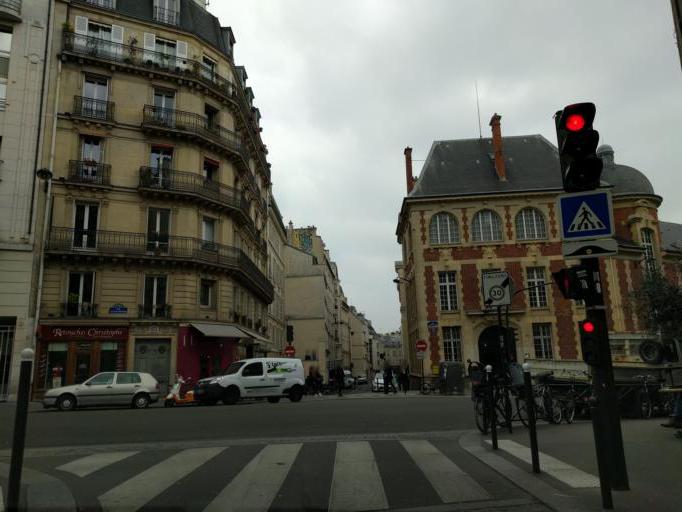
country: FR
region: Ile-de-France
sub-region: Paris
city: Paris
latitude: 48.8398
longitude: 2.3471
